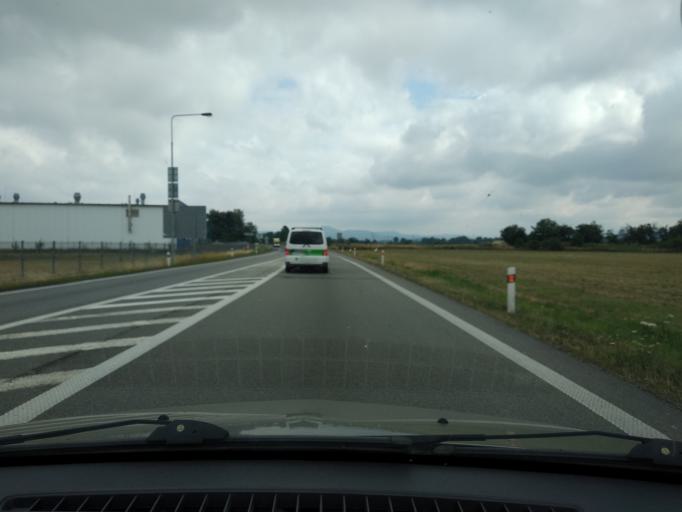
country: CZ
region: Olomoucky
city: Zabreh
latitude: 49.8770
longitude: 16.8924
